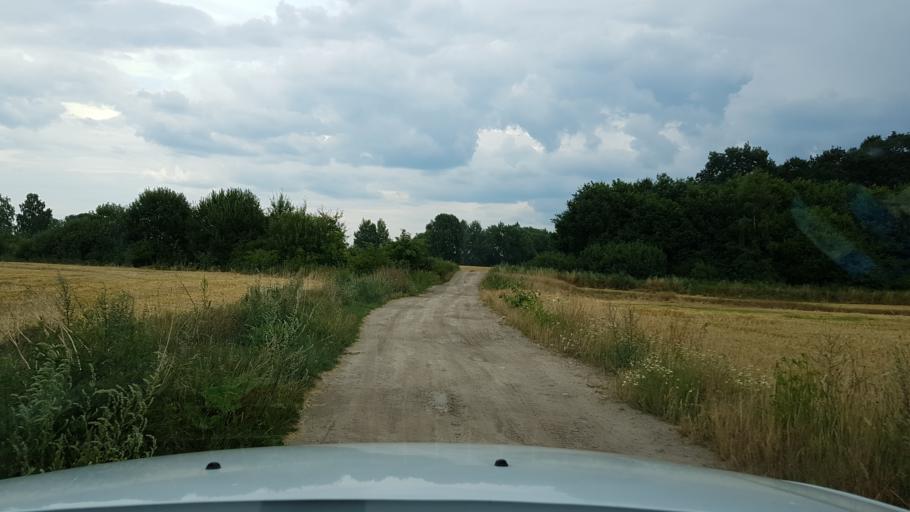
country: PL
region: West Pomeranian Voivodeship
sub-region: Powiat walecki
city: Walcz
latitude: 53.3735
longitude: 16.3460
